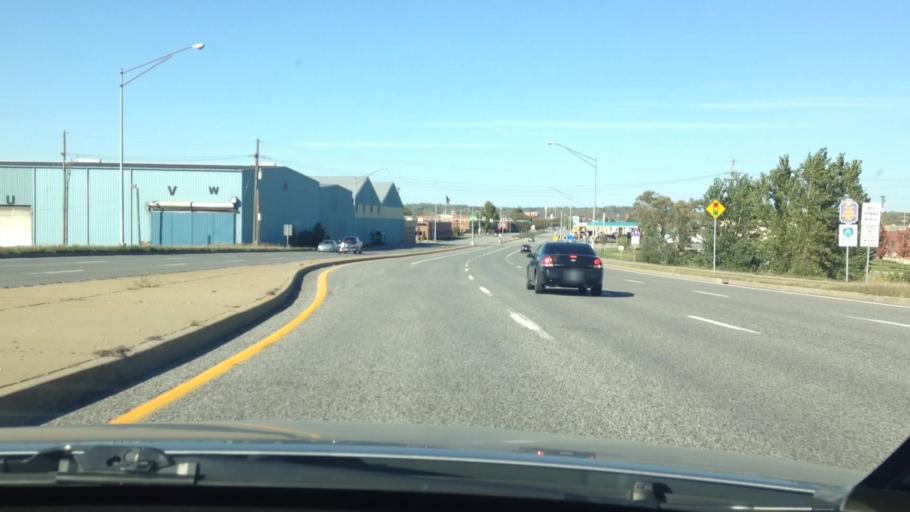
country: US
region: Missouri
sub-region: Clay County
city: North Kansas City
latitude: 39.1249
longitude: -94.5804
